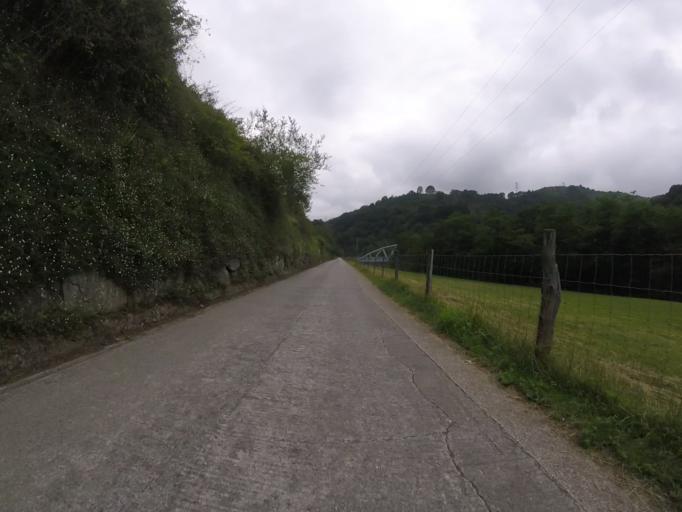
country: ES
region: Navarre
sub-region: Provincia de Navarra
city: Sunbilla
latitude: 43.1820
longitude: -1.6706
